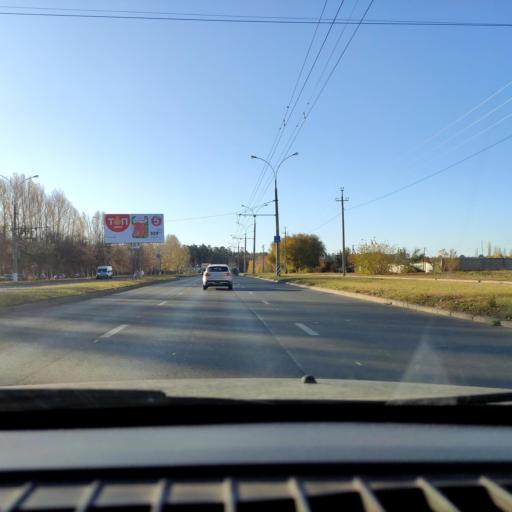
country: RU
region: Samara
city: Tol'yatti
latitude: 53.5022
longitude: 49.2990
